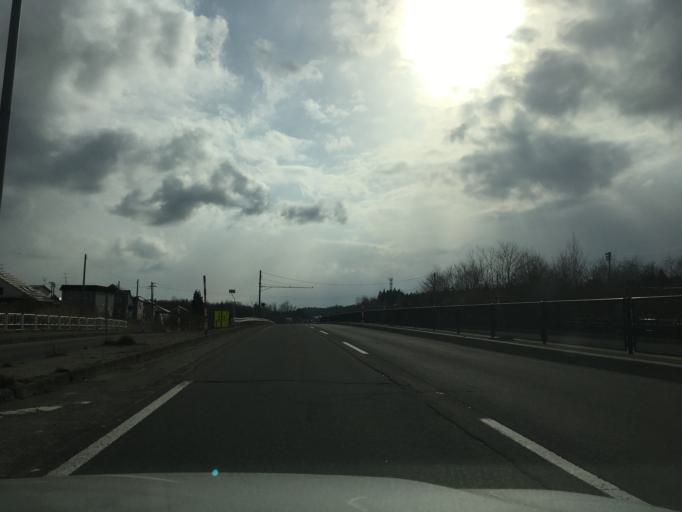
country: JP
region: Aomori
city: Aomori Shi
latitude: 40.8299
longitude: 140.6606
